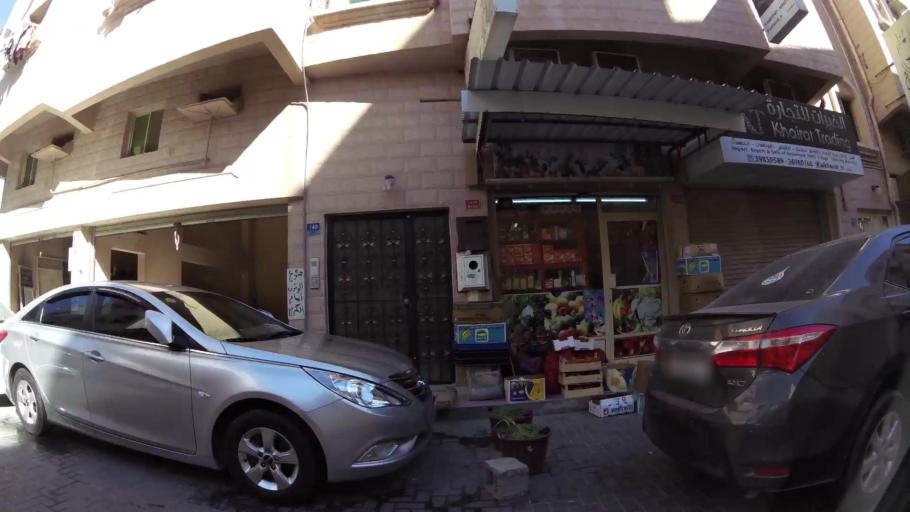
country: BH
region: Muharraq
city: Al Muharraq
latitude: 26.2576
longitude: 50.6152
